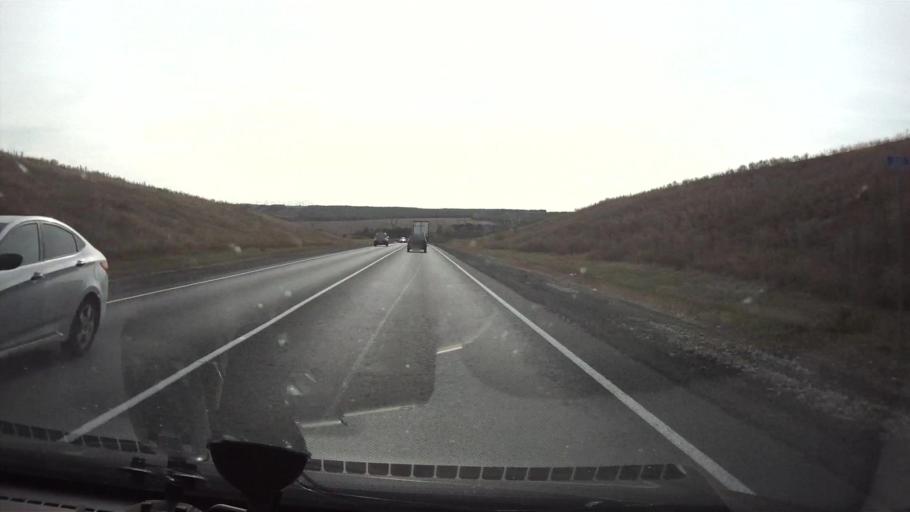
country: RU
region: Saratov
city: Sinodskoye
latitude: 51.9273
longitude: 46.5705
